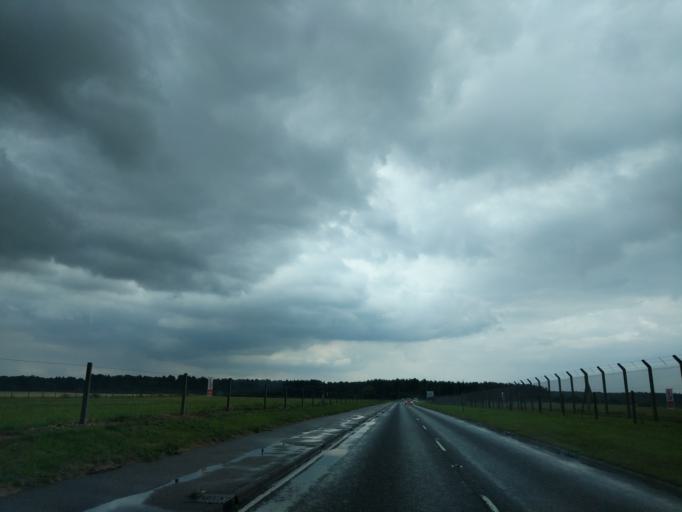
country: GB
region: England
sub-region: Suffolk
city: Lakenheath
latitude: 52.3624
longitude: 0.5082
